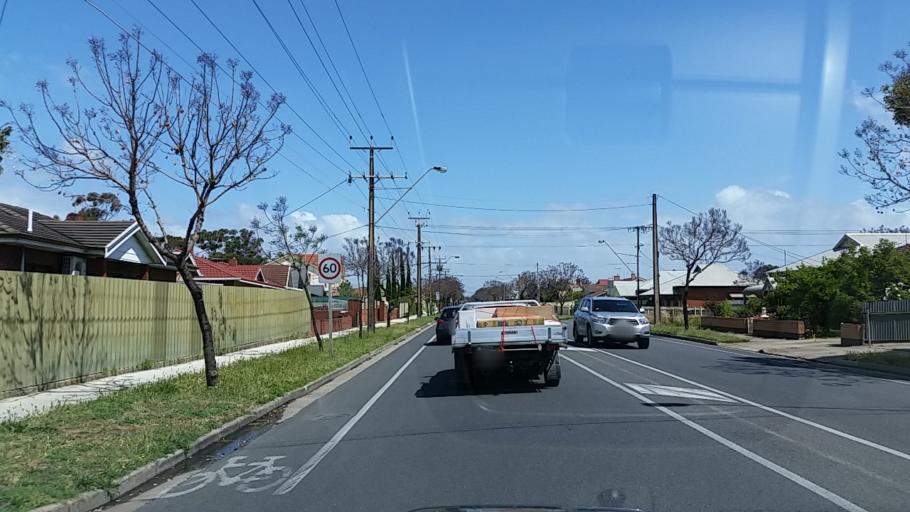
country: AU
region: South Australia
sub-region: Charles Sturt
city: Allenby Gardens
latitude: -34.8931
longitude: 138.5512
